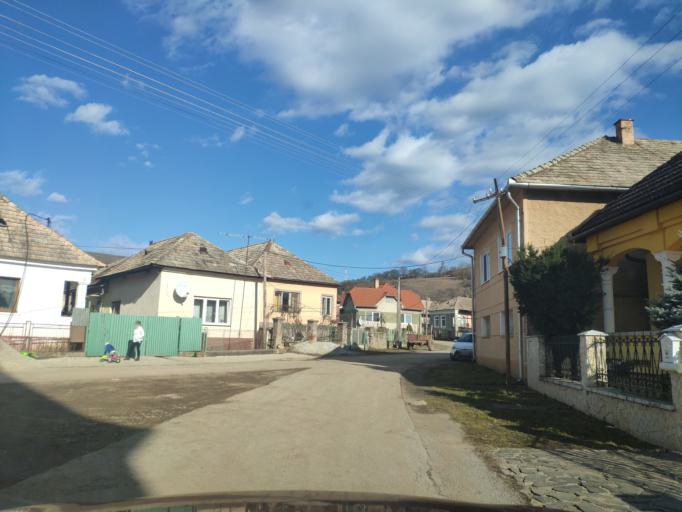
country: SK
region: Kosicky
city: Roznava
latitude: 48.5138
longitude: 20.3849
